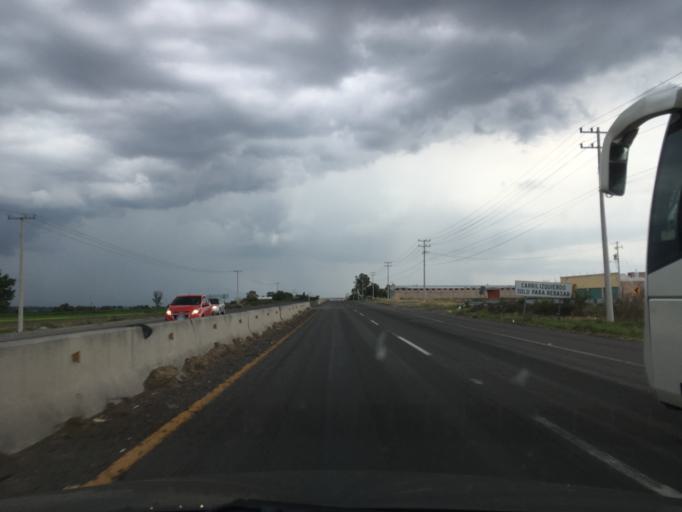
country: MX
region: Guanajuato
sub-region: Celaya
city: El Sauz (El Sauz de Villasenor)
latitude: 20.3941
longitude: -100.7899
